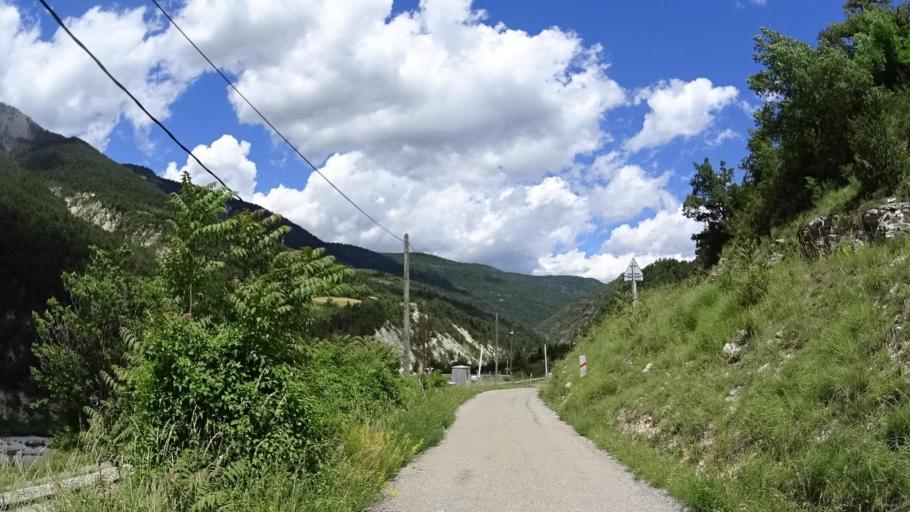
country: FR
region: Provence-Alpes-Cote d'Azur
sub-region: Departement des Alpes-de-Haute-Provence
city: Annot
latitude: 44.0244
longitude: 6.6271
